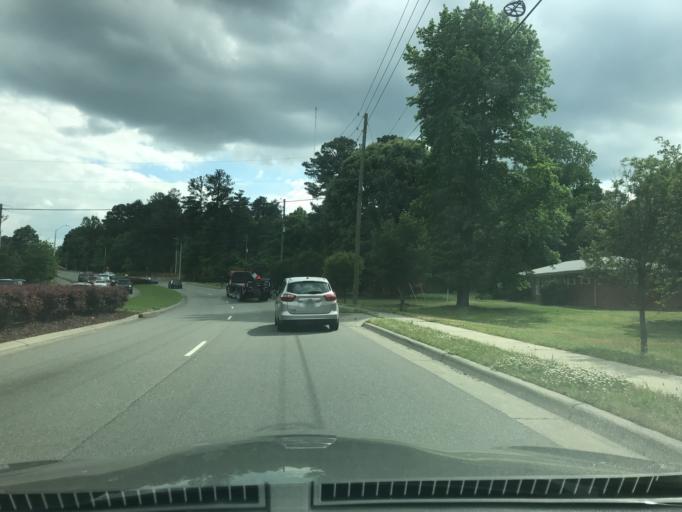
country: US
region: North Carolina
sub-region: Wake County
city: Wake Forest
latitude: 35.9288
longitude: -78.5867
